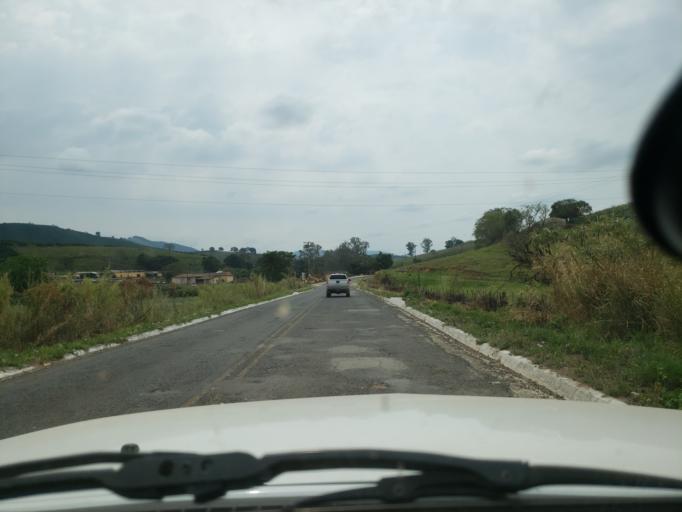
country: BR
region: Minas Gerais
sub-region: Jacutinga
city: Jacutinga
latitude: -22.2675
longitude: -46.6044
